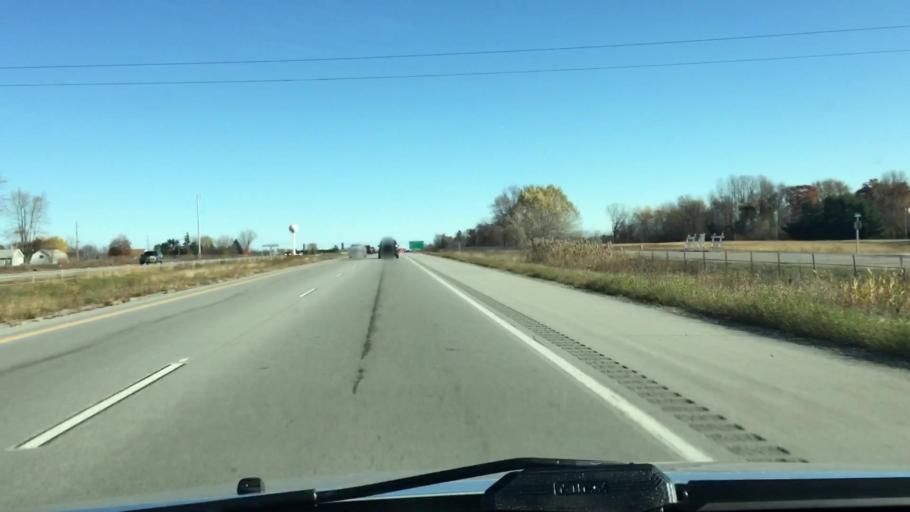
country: US
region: Wisconsin
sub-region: Brown County
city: Wrightstown
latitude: 44.4057
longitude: -88.1441
